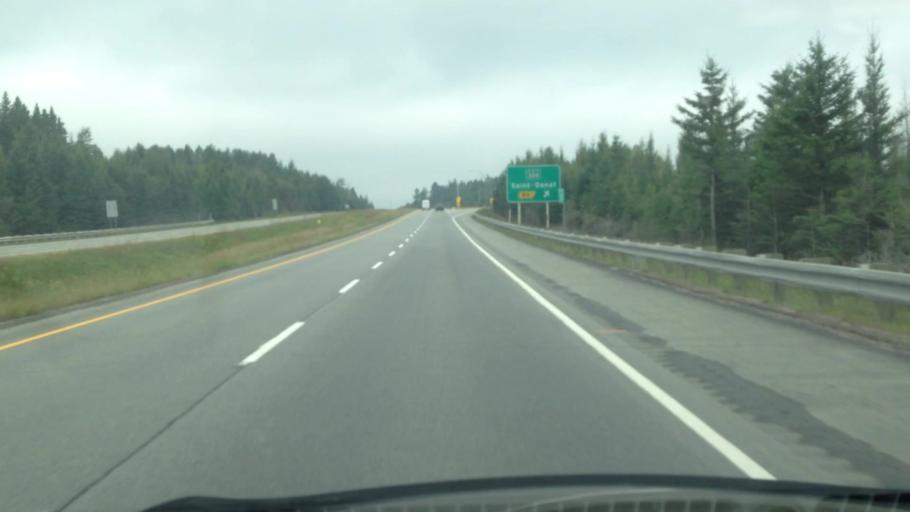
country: CA
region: Quebec
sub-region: Laurentides
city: Sainte-Agathe-des-Monts
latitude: 46.0618
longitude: -74.2808
